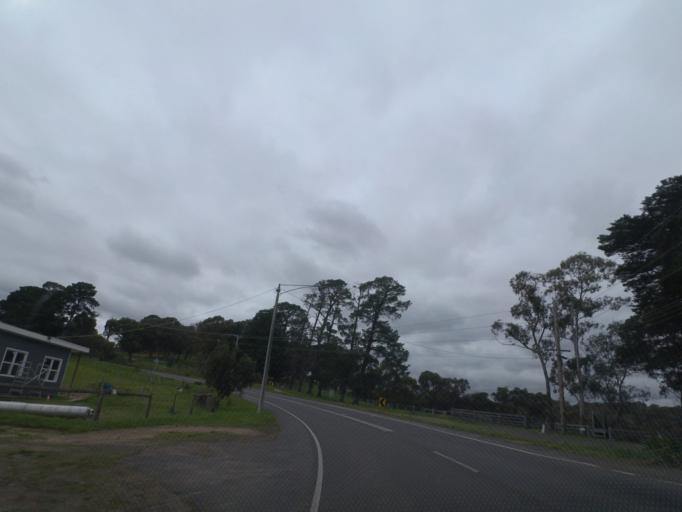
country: AU
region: Victoria
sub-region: Nillumbik
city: Hurstbridge
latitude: -37.6465
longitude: 145.2263
